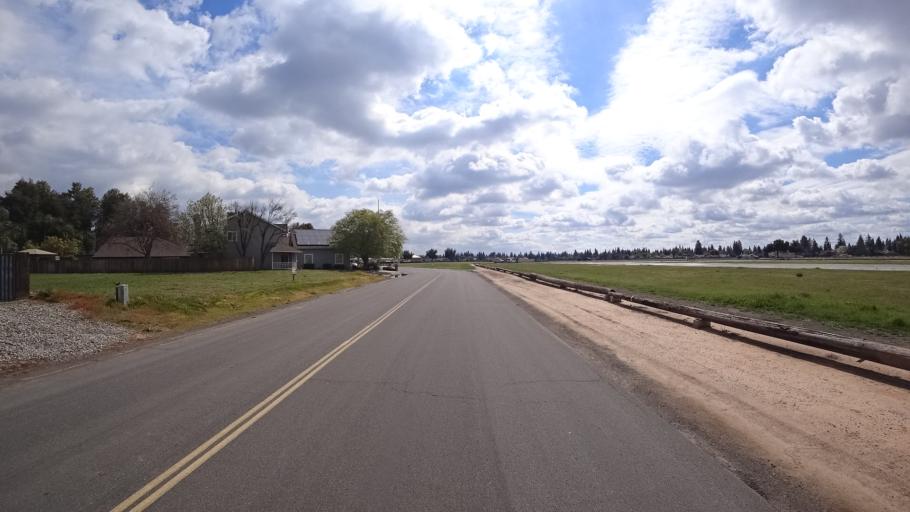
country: US
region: California
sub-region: Fresno County
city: West Park
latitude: 36.8390
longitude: -119.8669
